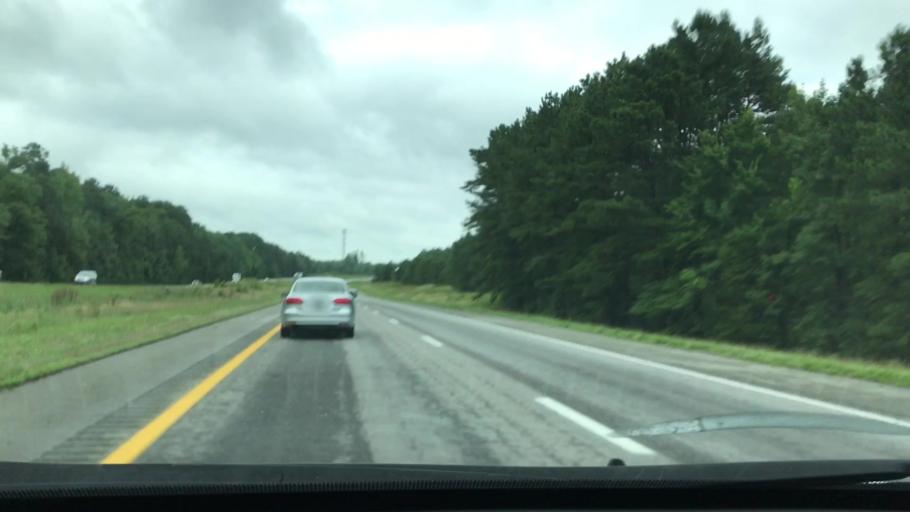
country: US
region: Virginia
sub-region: City of Emporia
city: Emporia
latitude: 36.8187
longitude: -77.4553
